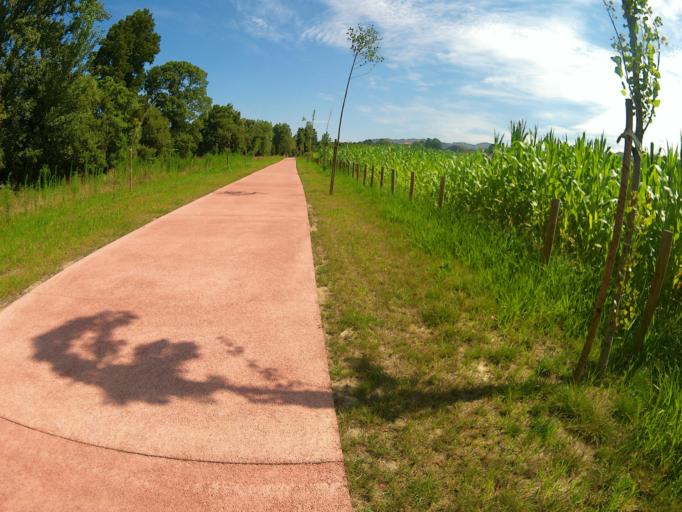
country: PT
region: Viana do Castelo
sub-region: Vila Nova de Cerveira
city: Vila Nova de Cerveira
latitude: 41.9175
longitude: -8.7789
